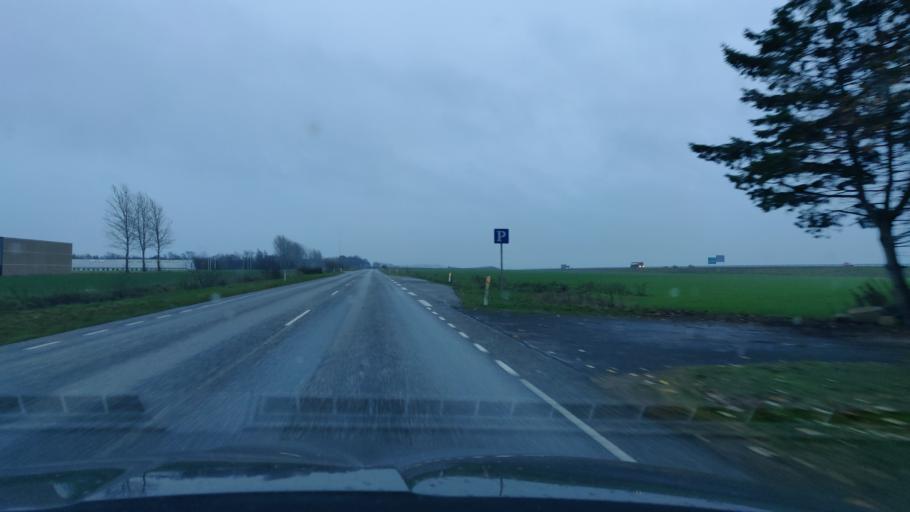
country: DK
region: Central Jutland
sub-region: Herning Kommune
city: Avlum
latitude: 56.2534
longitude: 8.7905
